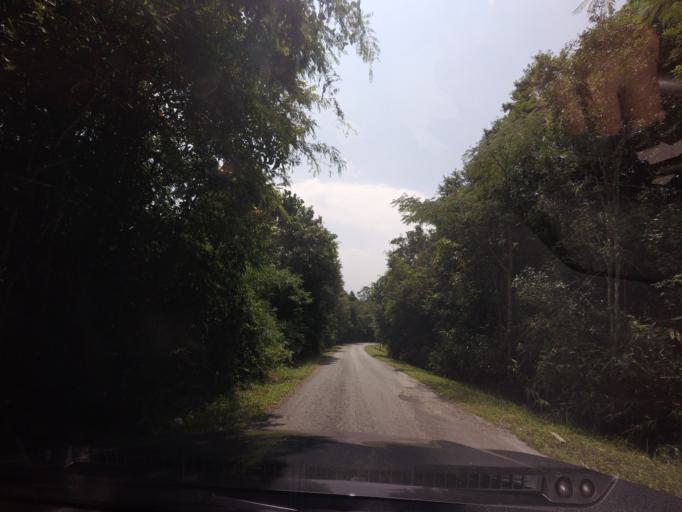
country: TH
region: Loei
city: Phu Ruea
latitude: 17.4832
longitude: 101.3540
